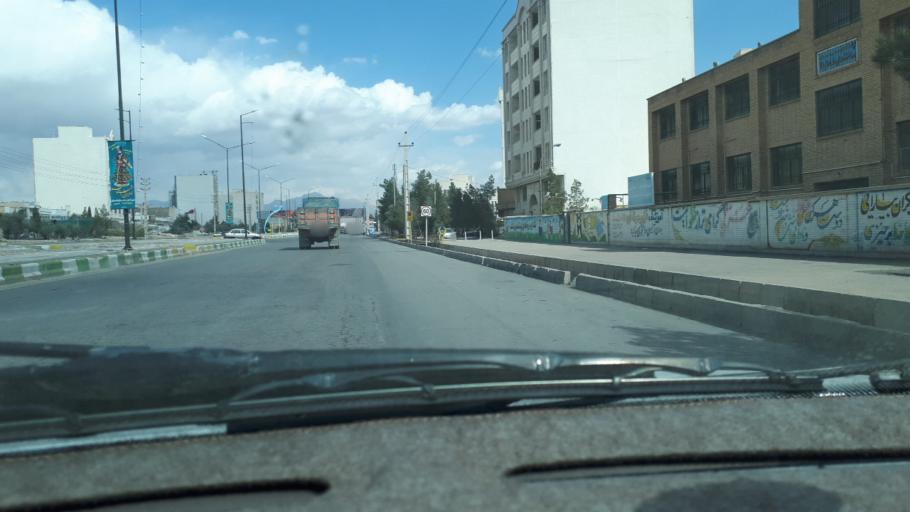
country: IR
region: Semnan
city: Semnan
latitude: 35.5827
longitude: 53.3752
